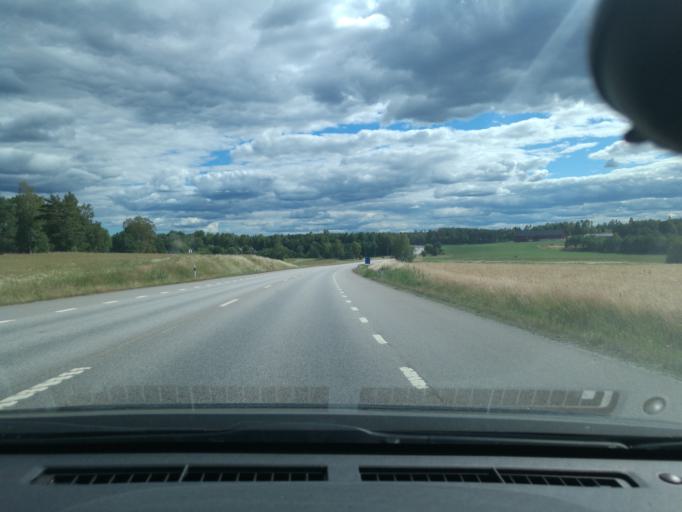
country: SE
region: OEstergoetland
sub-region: Soderkopings Kommun
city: Soederkoeping
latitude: 58.4570
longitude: 16.3659
